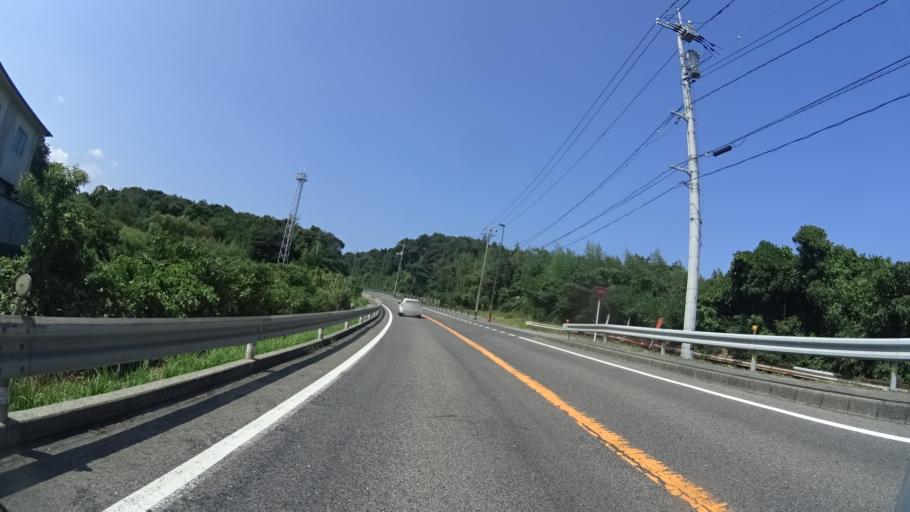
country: JP
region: Shimane
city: Masuda
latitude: 34.6746
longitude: 131.7210
